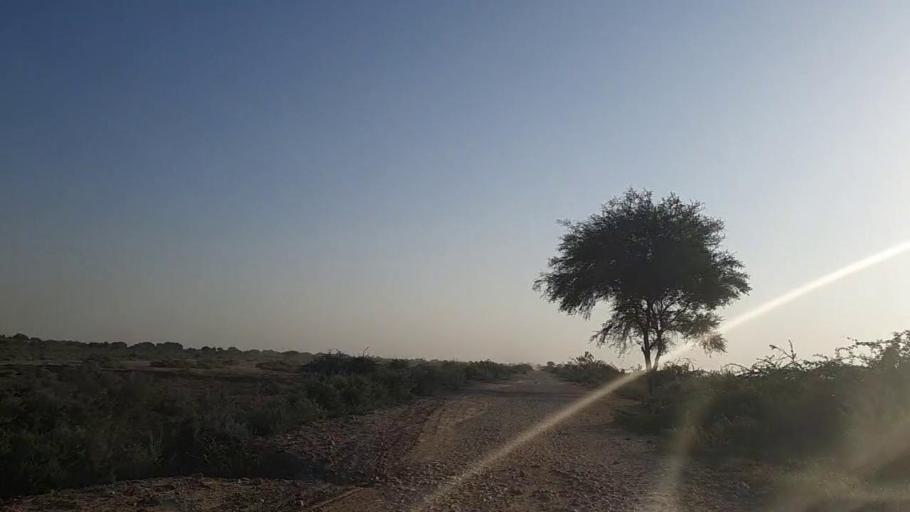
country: PK
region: Sindh
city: Jati
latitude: 24.4411
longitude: 68.1941
